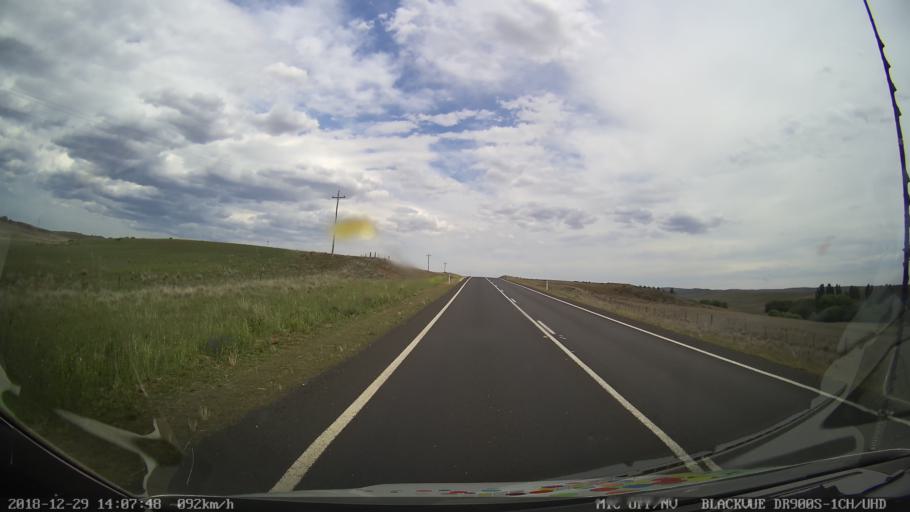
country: AU
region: New South Wales
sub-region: Cooma-Monaro
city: Cooma
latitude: -36.3567
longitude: 149.2148
